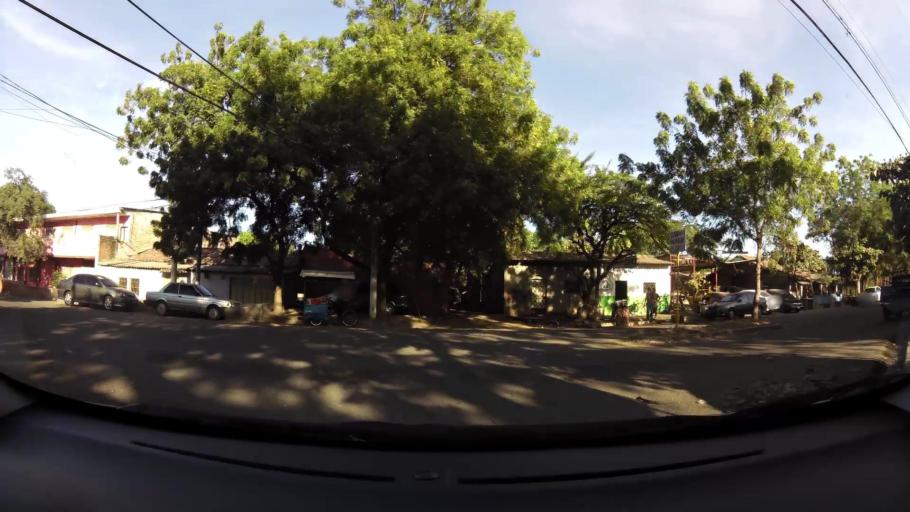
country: SV
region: San Miguel
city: San Miguel
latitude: 13.4679
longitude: -88.1786
